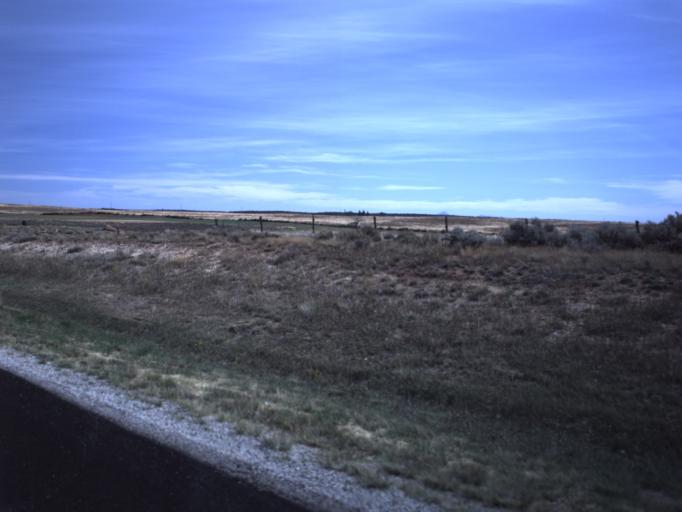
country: US
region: Utah
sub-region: San Juan County
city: Monticello
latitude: 37.8539
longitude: -109.1813
